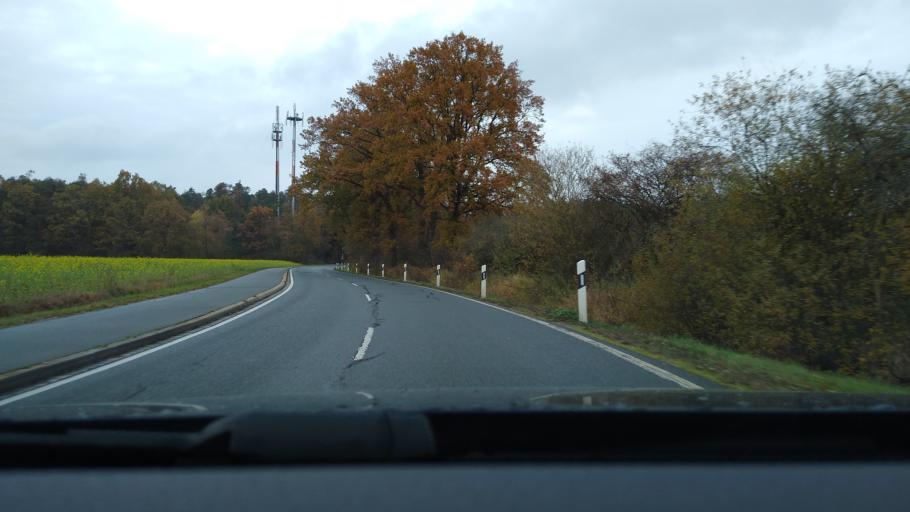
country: DE
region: Bavaria
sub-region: Regierungsbezirk Mittelfranken
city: Wetzendorf
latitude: 49.5249
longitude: 11.0592
